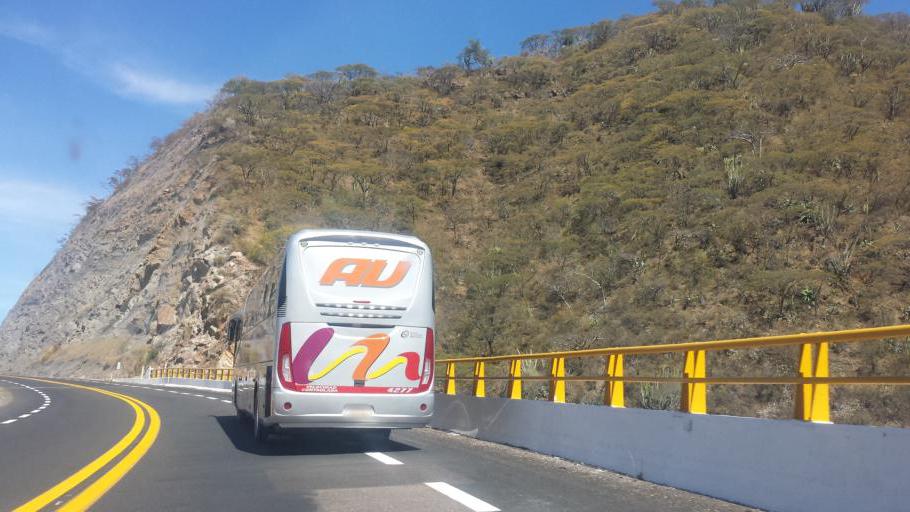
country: MX
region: Puebla
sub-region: San Jose Miahuatlan
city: San Pedro Tetitlan
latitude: 18.0915
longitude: -97.3393
